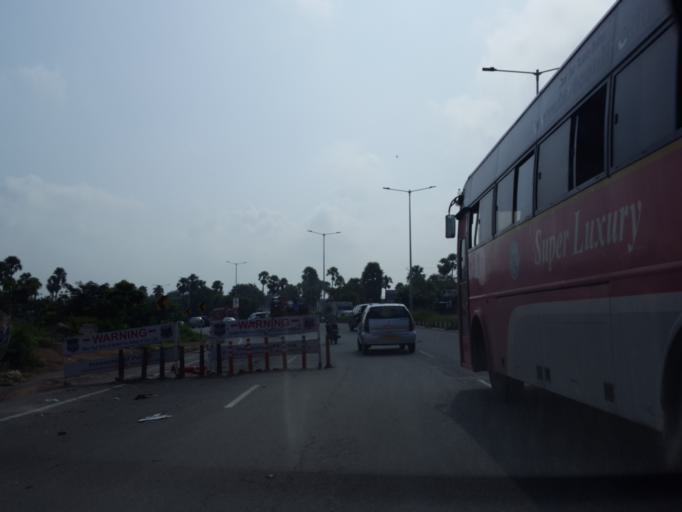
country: IN
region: Telangana
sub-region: Rangareddi
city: Ghatkesar
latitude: 17.3066
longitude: 78.7047
